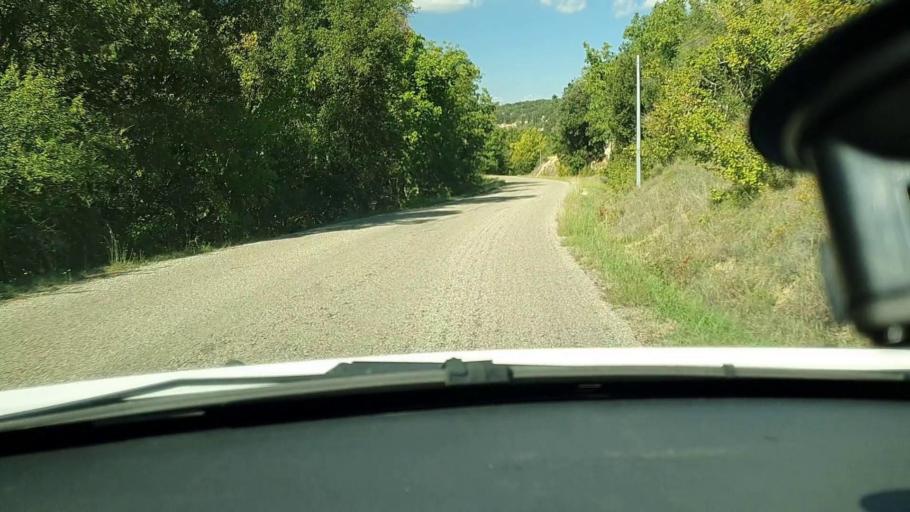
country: FR
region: Languedoc-Roussillon
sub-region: Departement du Gard
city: Goudargues
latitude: 44.1674
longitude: 4.3901
